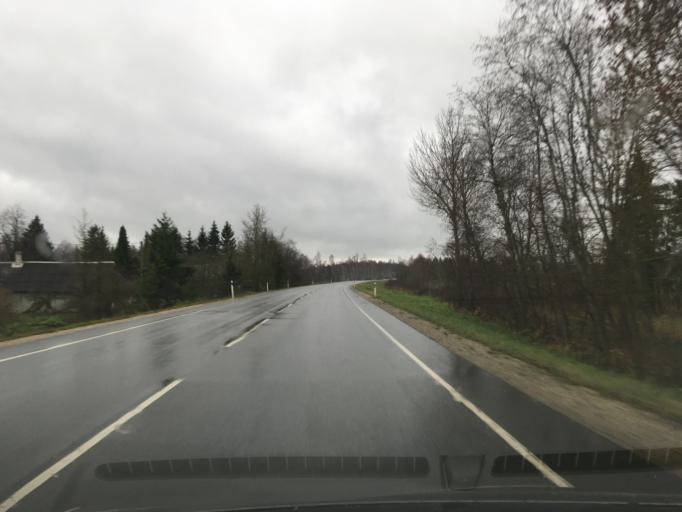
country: EE
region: Laeaene
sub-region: Lihula vald
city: Lihula
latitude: 58.7935
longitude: 24.0406
